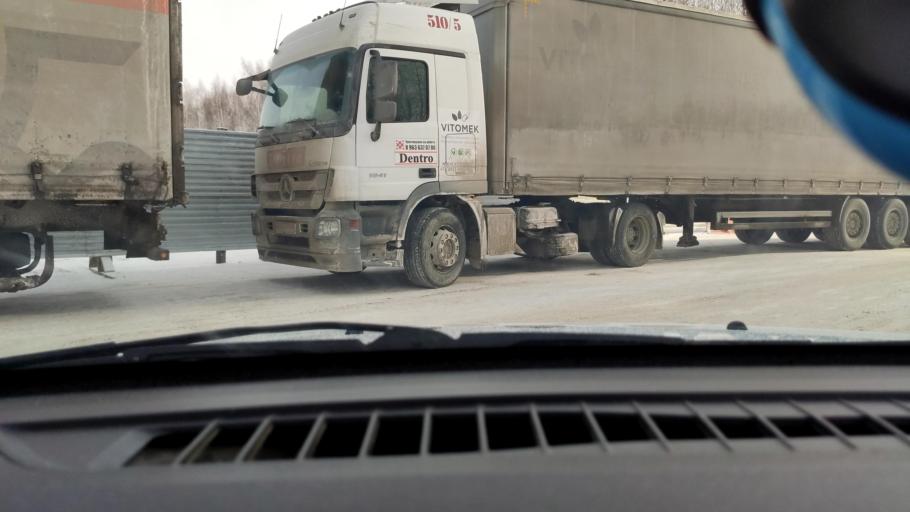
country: RU
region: Perm
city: Overyata
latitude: 58.0185
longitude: 55.9225
